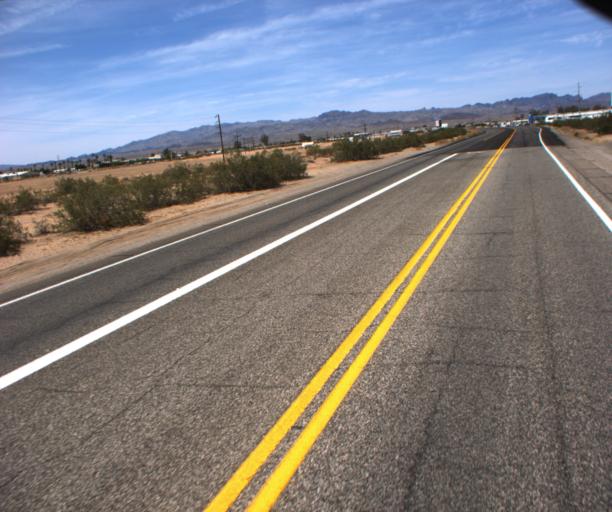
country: US
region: Arizona
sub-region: La Paz County
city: Parker
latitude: 34.1309
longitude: -114.2798
